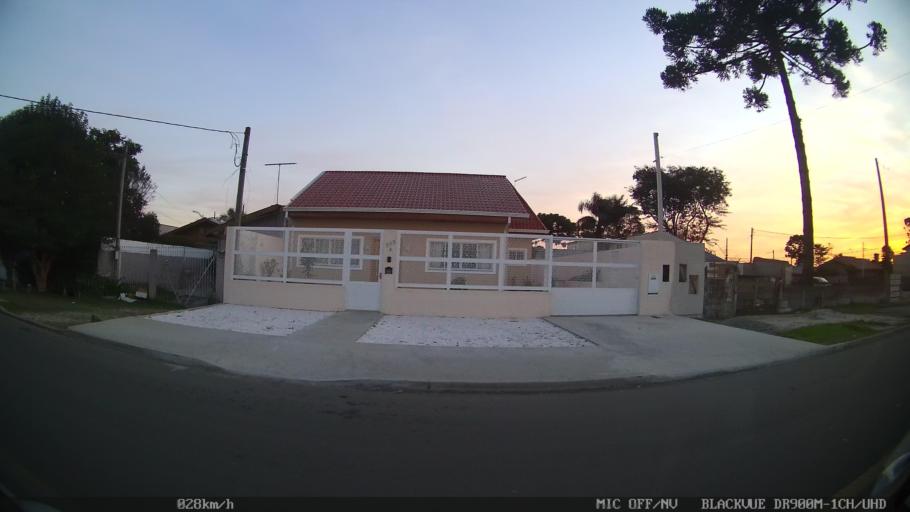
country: BR
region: Parana
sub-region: Pinhais
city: Pinhais
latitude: -25.4423
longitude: -49.1979
